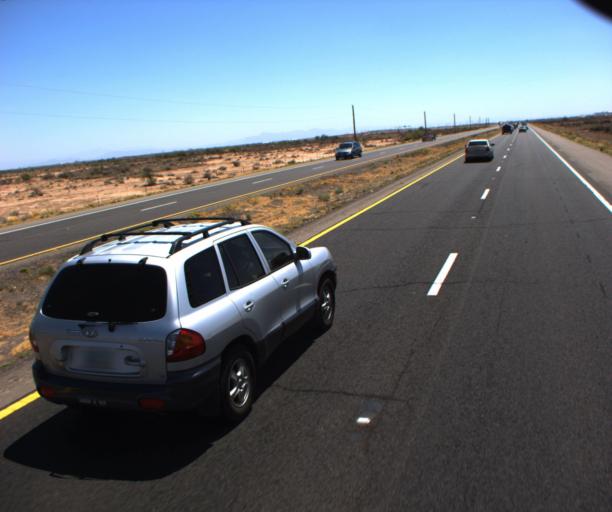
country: US
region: Arizona
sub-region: Maricopa County
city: Sun Lakes
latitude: 33.2520
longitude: -111.9667
